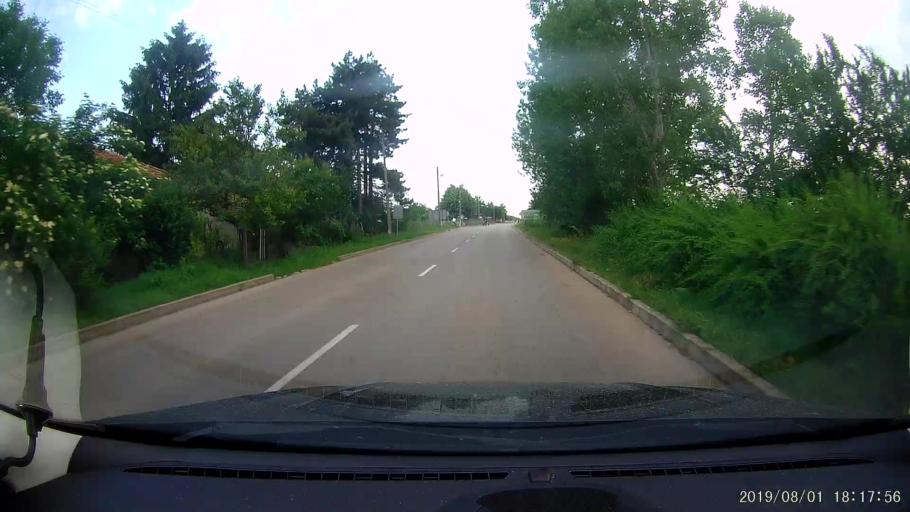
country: BG
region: Shumen
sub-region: Obshtina Kaolinovo
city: Kaolinovo
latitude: 43.7038
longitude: 27.0809
